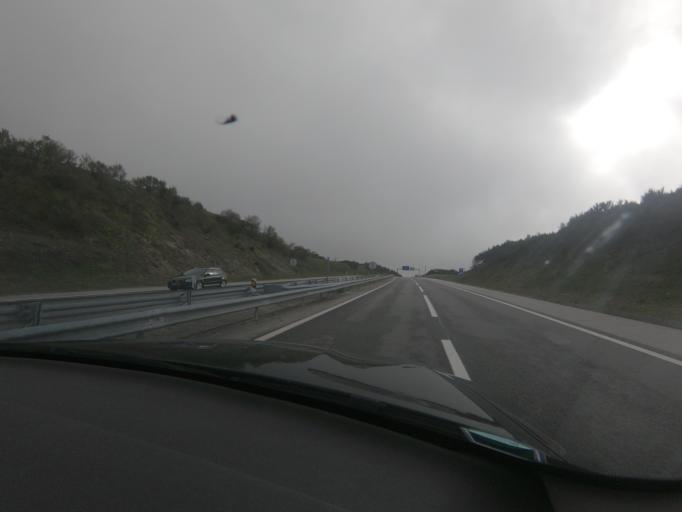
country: PT
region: Viseu
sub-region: Tarouca
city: Tarouca
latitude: 41.0101
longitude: -7.8842
